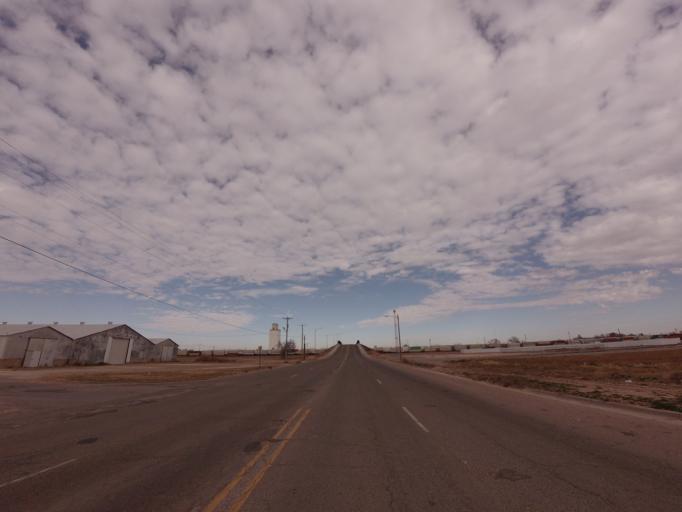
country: US
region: New Mexico
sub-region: Curry County
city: Clovis
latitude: 34.3953
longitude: -103.2205
